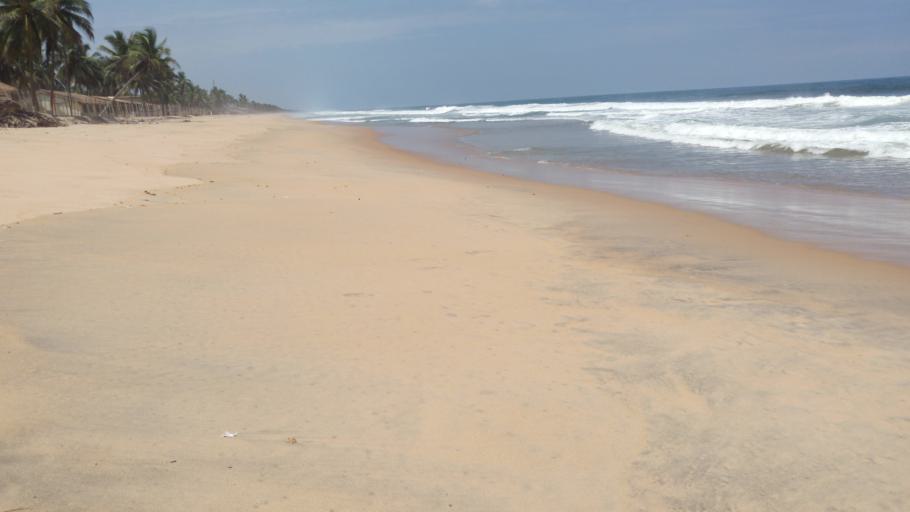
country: CI
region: Sud-Comoe
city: Grand-Bassam
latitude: 5.1876
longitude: -3.6960
